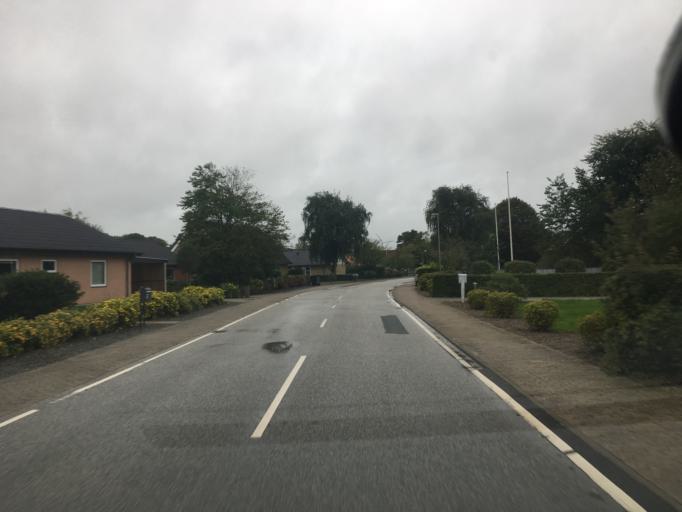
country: DE
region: Schleswig-Holstein
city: Ellhoft
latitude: 54.9391
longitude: 8.9640
